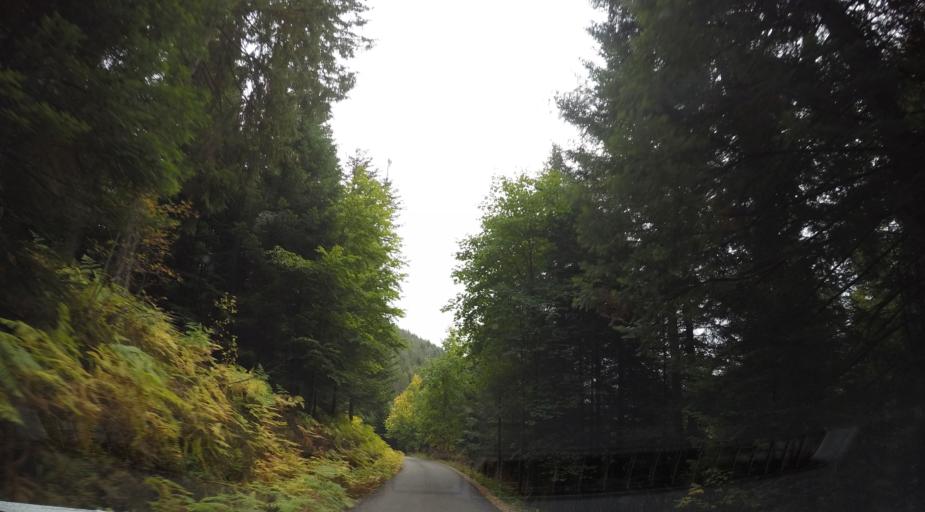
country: DE
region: Baden-Wuerttemberg
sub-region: Karlsruhe Region
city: Baiersbronn
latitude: 48.5477
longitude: 8.3496
